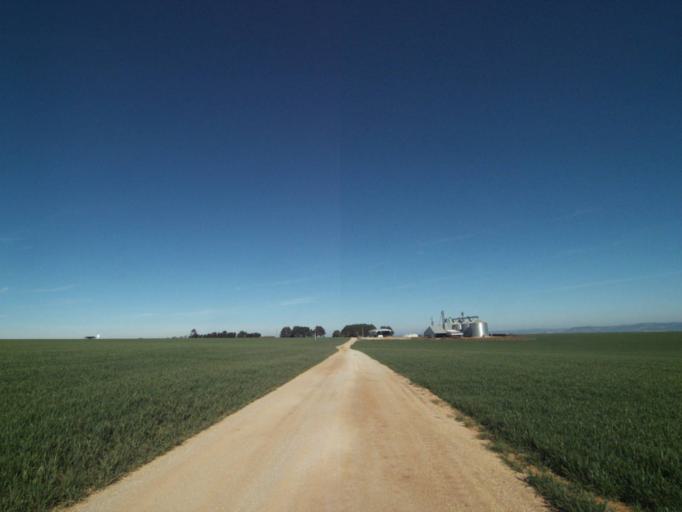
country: BR
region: Parana
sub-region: Tibagi
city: Tibagi
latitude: -24.5387
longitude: -50.3028
